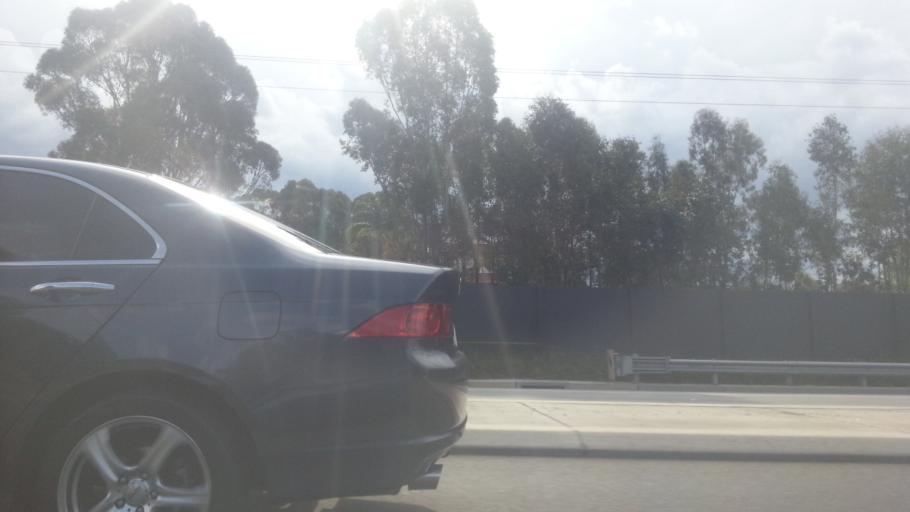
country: AU
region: New South Wales
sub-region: Penrith Municipality
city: Werrington Downs
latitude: -33.7310
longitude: 150.7189
